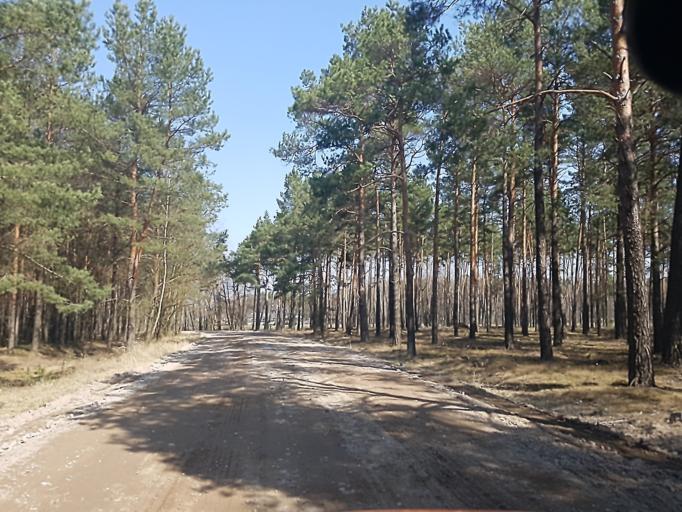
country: DE
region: Brandenburg
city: Forst
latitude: 51.6721
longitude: 14.5725
